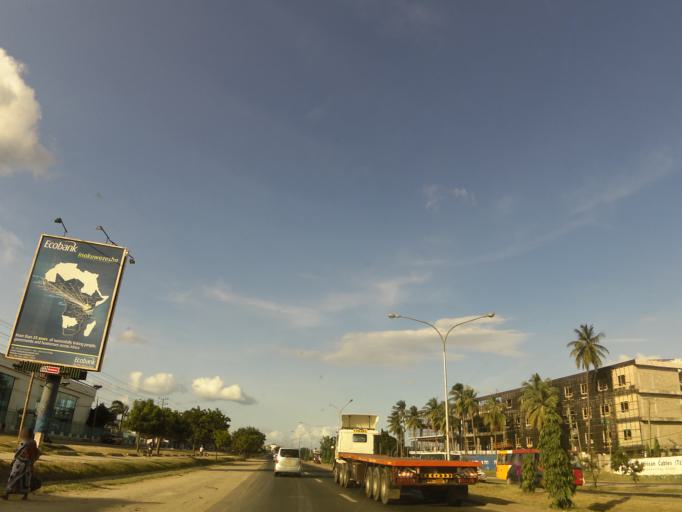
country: TZ
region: Dar es Salaam
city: Dar es Salaam
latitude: -6.8510
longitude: 39.2314
